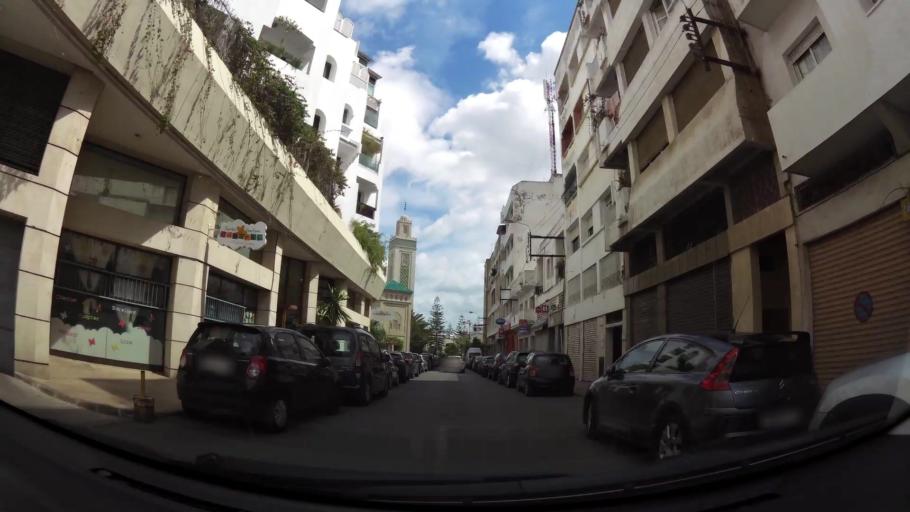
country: MA
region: Grand Casablanca
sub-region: Casablanca
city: Casablanca
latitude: 33.5763
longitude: -7.6512
